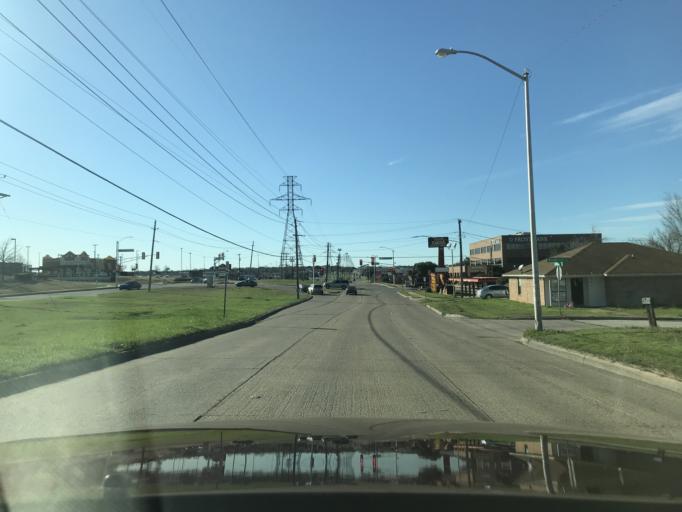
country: US
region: Texas
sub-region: Tarrant County
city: Edgecliff Village
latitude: 32.6492
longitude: -97.3593
